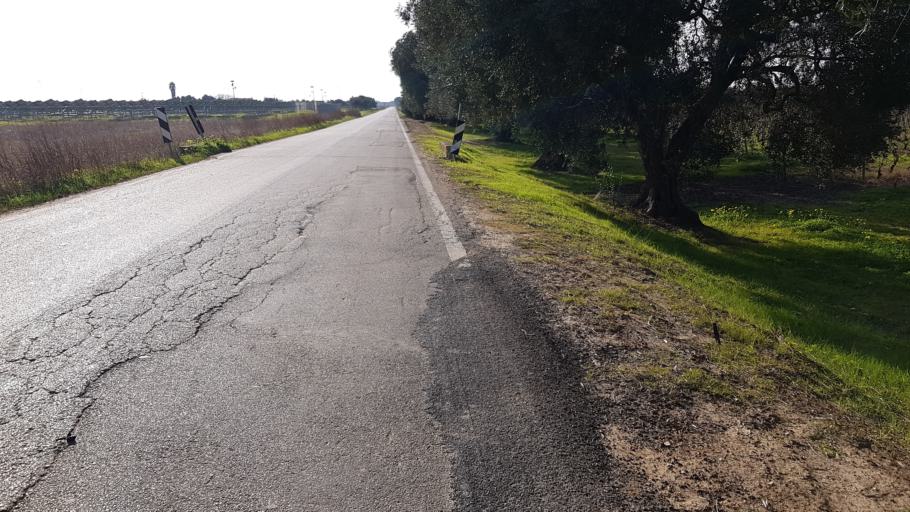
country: IT
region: Apulia
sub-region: Provincia di Brindisi
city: La Rosa
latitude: 40.5854
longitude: 17.9026
